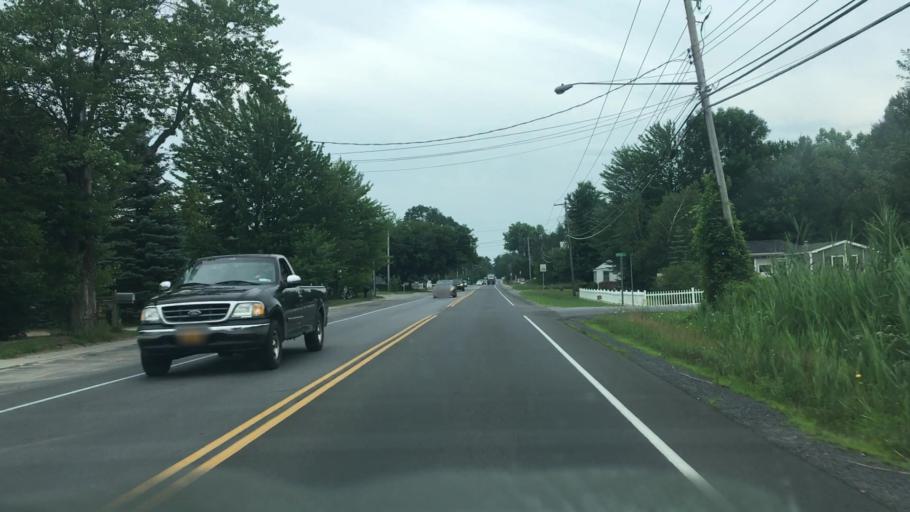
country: US
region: New York
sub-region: Clinton County
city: Plattsburgh West
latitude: 44.6825
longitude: -73.5066
